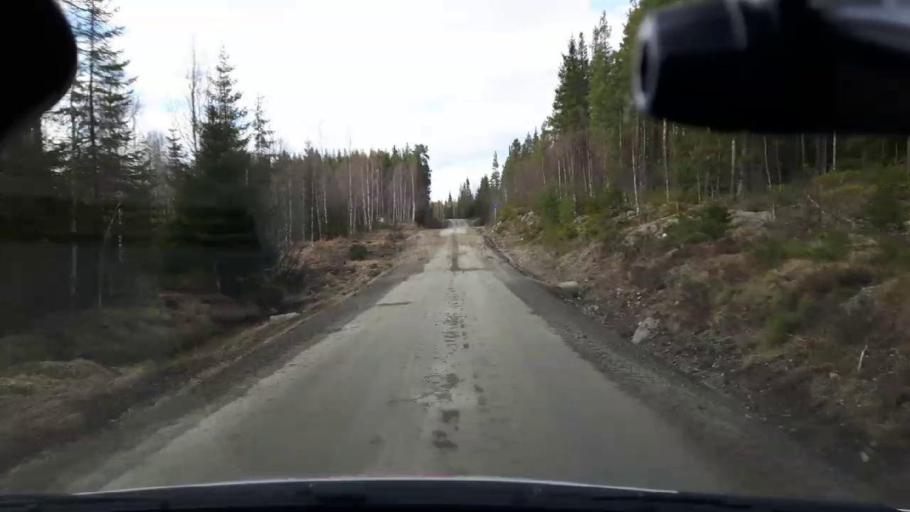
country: SE
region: Jaemtland
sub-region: Bergs Kommun
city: Hoverberg
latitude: 62.8897
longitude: 14.6574
